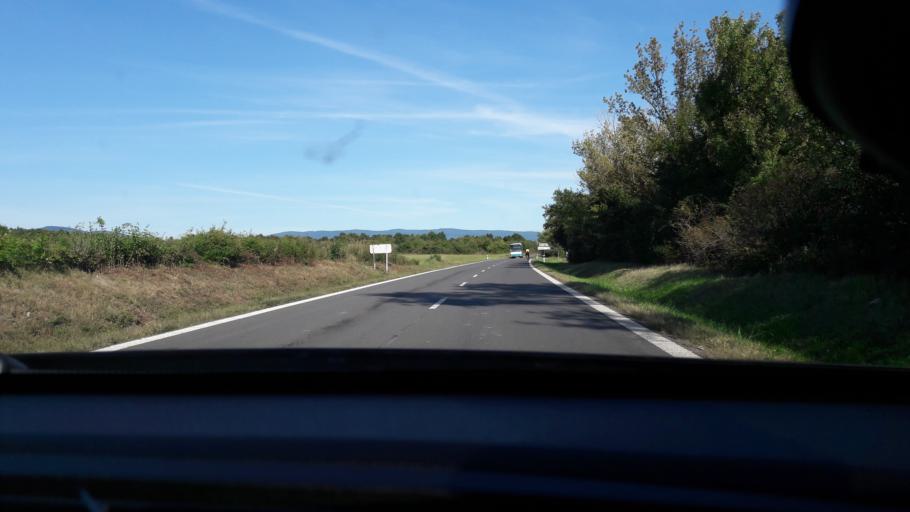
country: SK
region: Kosicky
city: Vinne
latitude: 48.8106
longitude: 22.0353
